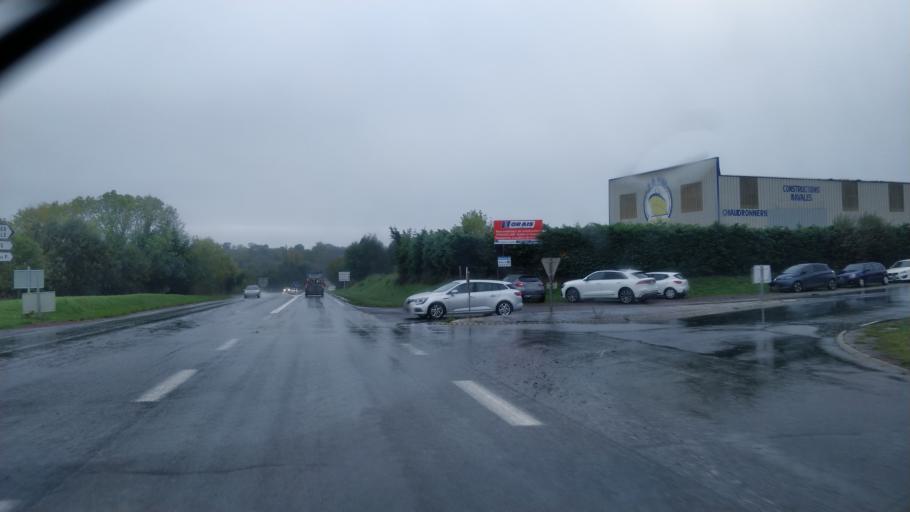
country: FR
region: Lower Normandy
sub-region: Departement de la Manche
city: Saint-Planchers
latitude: 48.8546
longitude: -1.5392
